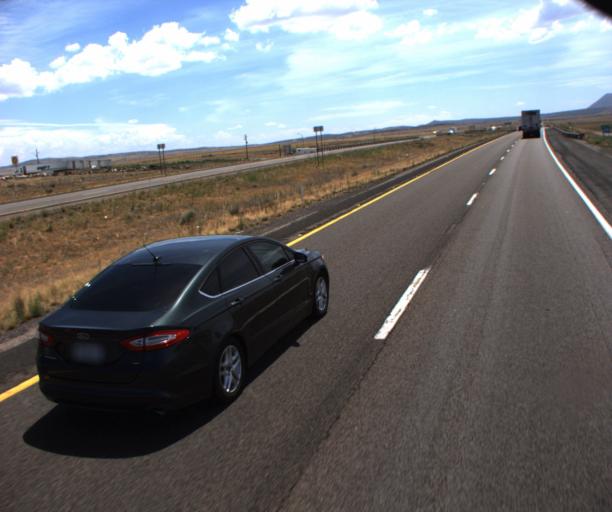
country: US
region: Arizona
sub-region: Yavapai County
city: Paulden
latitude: 35.3114
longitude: -112.8581
